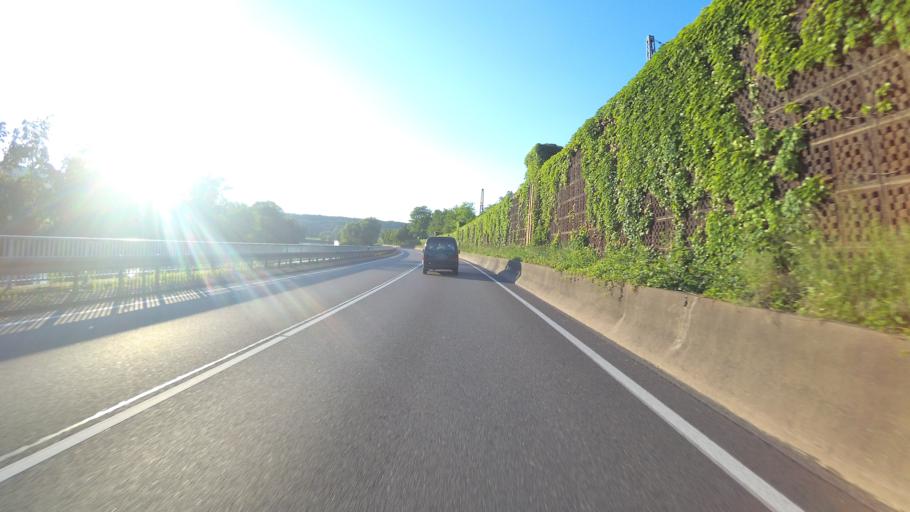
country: DE
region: Saarland
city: Kleinblittersdorf
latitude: 49.1642
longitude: 7.0335
